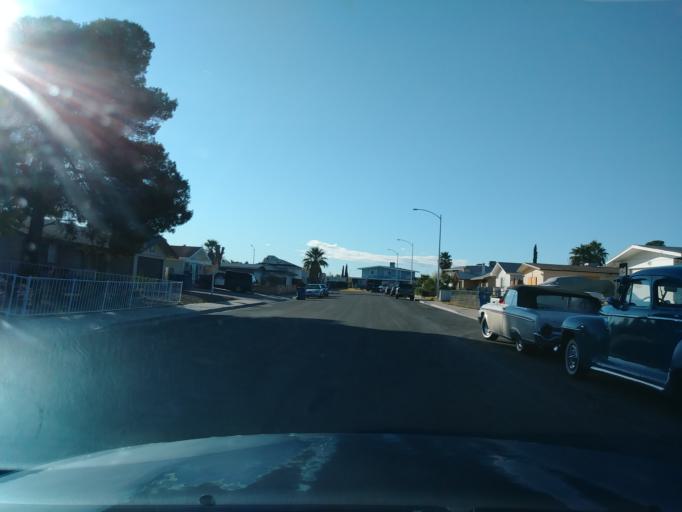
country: US
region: Nevada
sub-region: Clark County
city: Spring Valley
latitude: 36.1655
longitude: -115.2483
